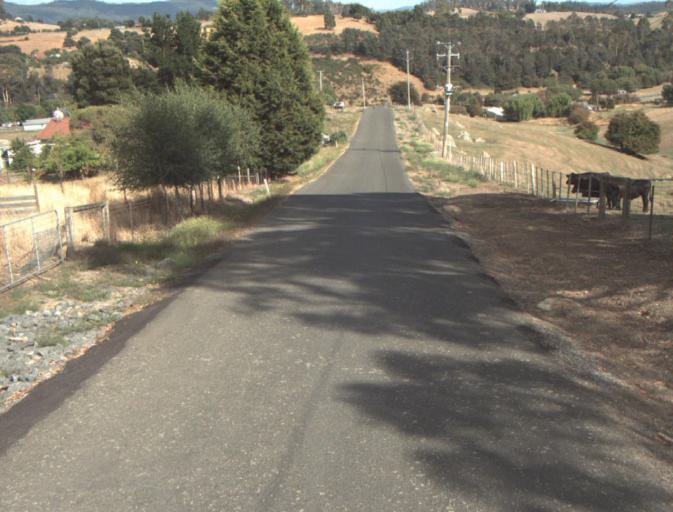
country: AU
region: Tasmania
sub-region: Launceston
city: Mayfield
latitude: -41.2624
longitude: 147.2228
